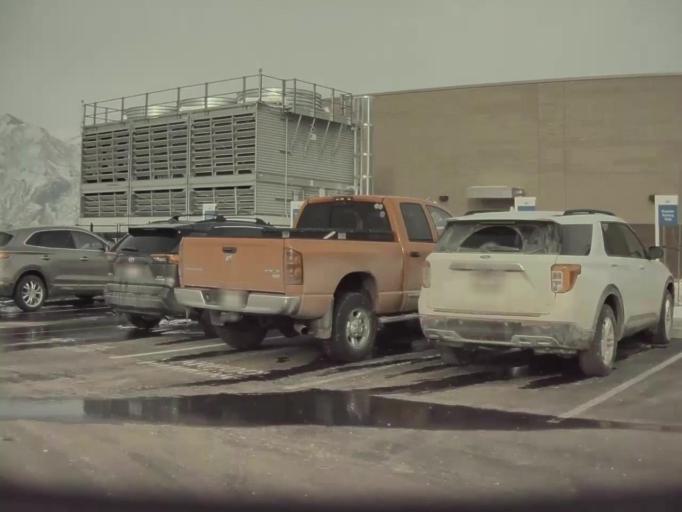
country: US
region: Utah
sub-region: Utah County
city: Spanish Fork
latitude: 40.1315
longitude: -111.6413
